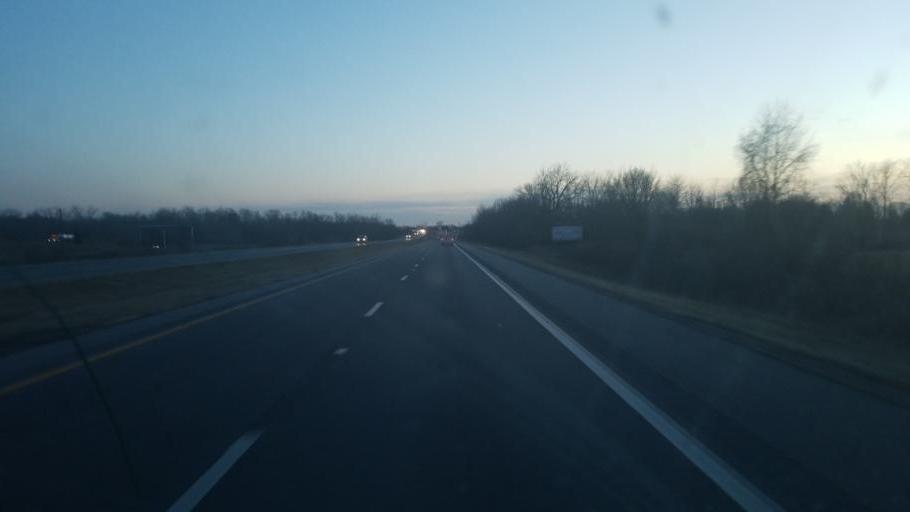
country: US
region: Ohio
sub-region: Marion County
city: Prospect
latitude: 40.4706
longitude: -83.0750
